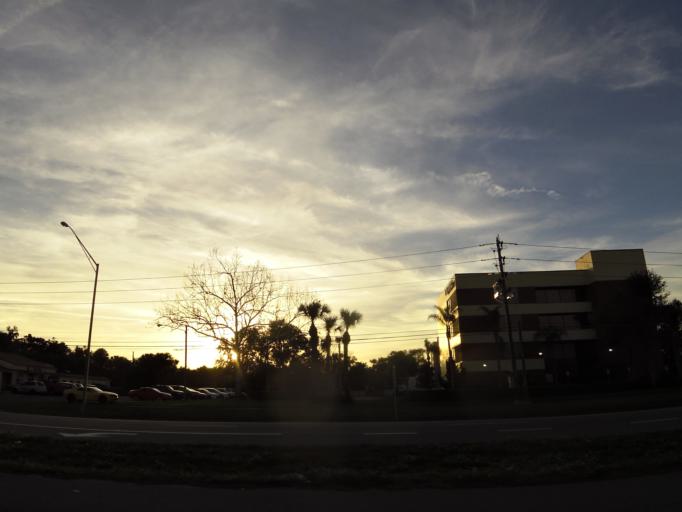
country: US
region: Florida
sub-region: Volusia County
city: De Land Southwest
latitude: 29.0030
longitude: -81.3026
